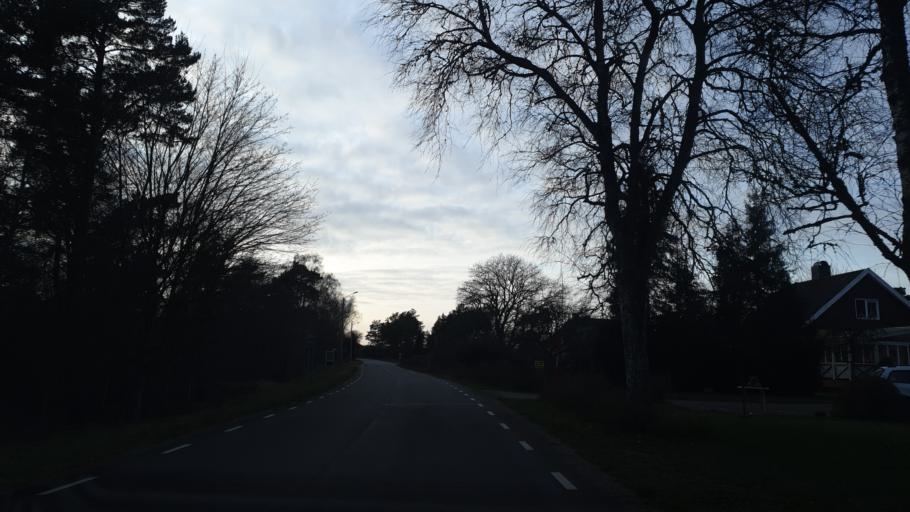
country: SE
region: Blekinge
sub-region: Karlskrona Kommun
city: Jaemjoe
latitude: 56.2154
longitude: 15.9753
